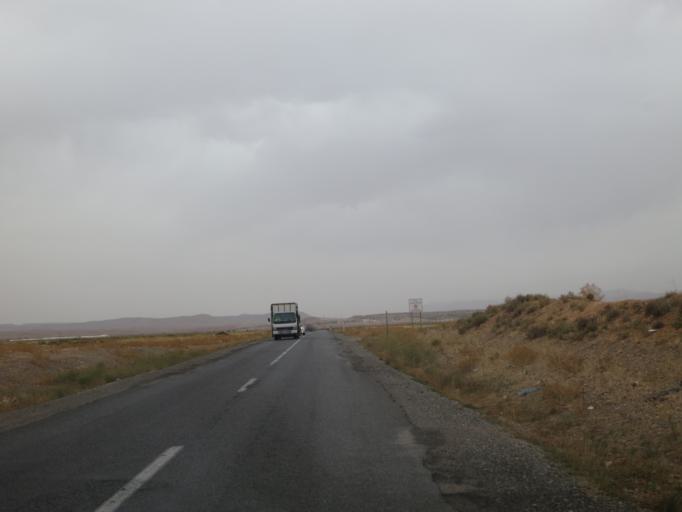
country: MA
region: Meknes-Tafilalet
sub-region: Khenifra
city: Midelt
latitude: 32.6975
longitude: -4.8266
